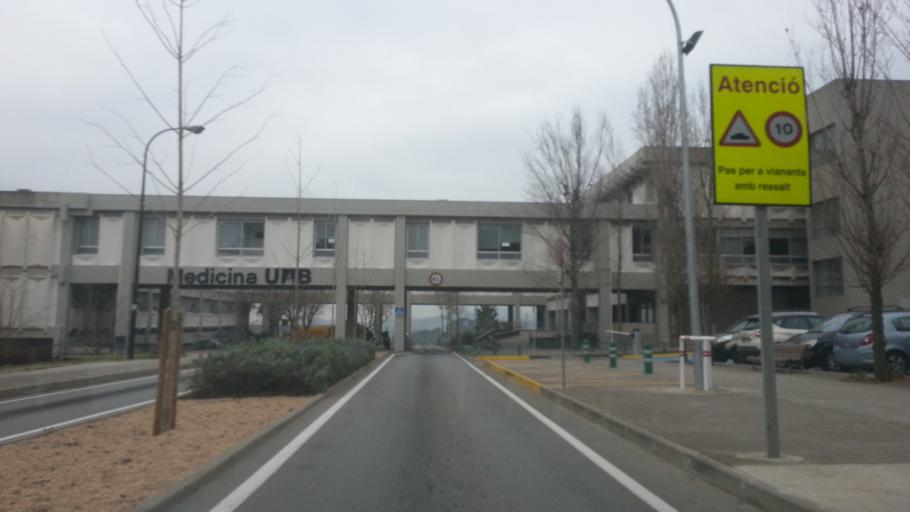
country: ES
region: Catalonia
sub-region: Provincia de Barcelona
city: Barbera del Valles
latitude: 41.4987
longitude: 2.1053
